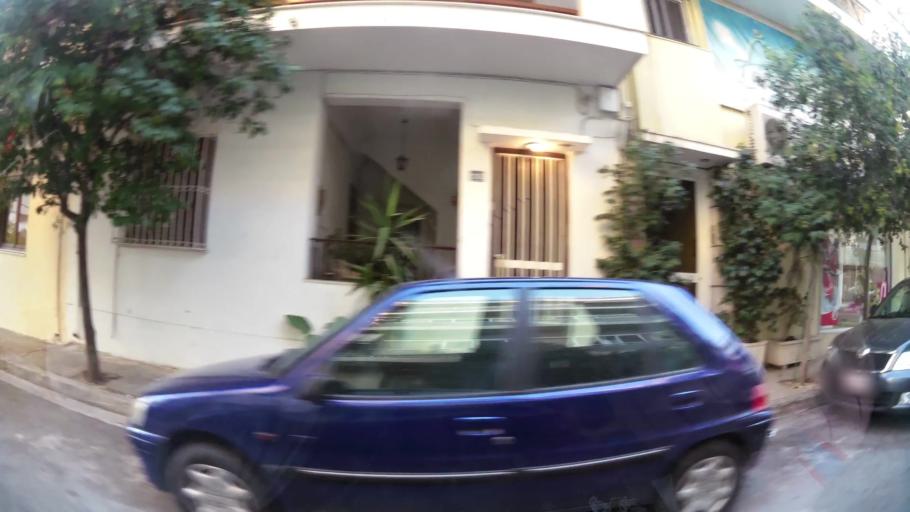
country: GR
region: Attica
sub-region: Nomos Piraios
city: Nikaia
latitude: 37.9717
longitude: 23.6420
